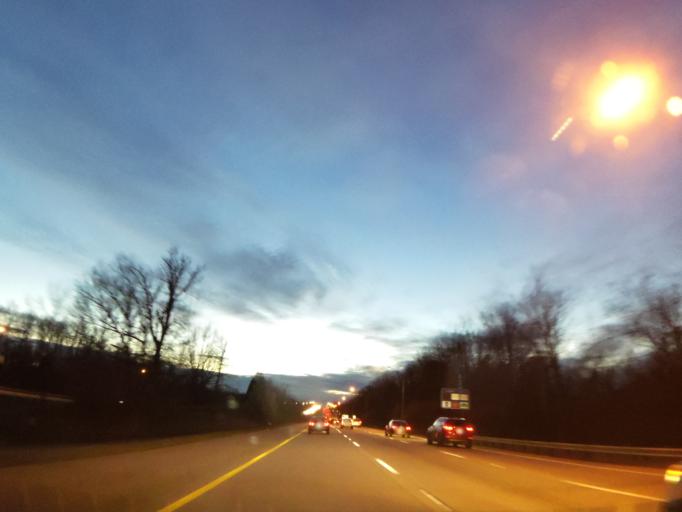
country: US
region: Kentucky
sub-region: Jefferson County
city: Middletown
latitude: 38.2232
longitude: -85.5172
